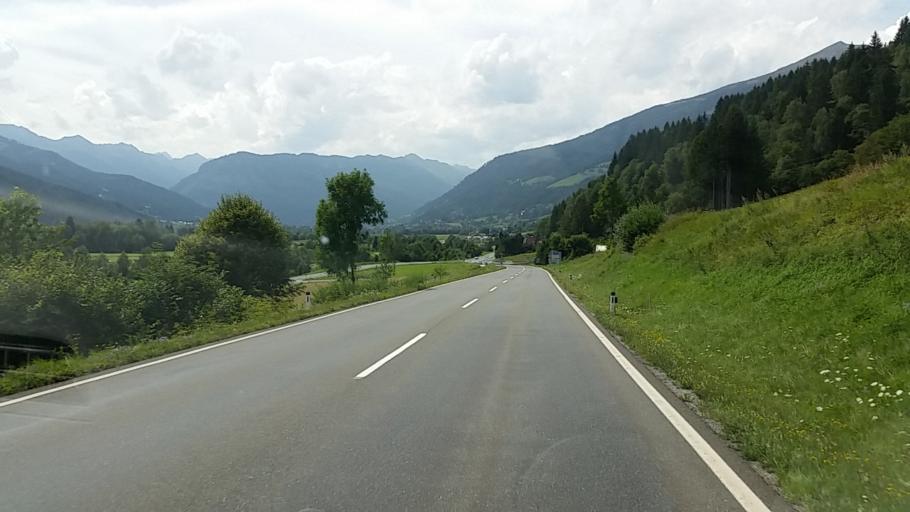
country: AT
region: Salzburg
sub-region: Politischer Bezirk Tamsweg
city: Sankt Margarethen im Lungau
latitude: 47.0922
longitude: 13.6831
